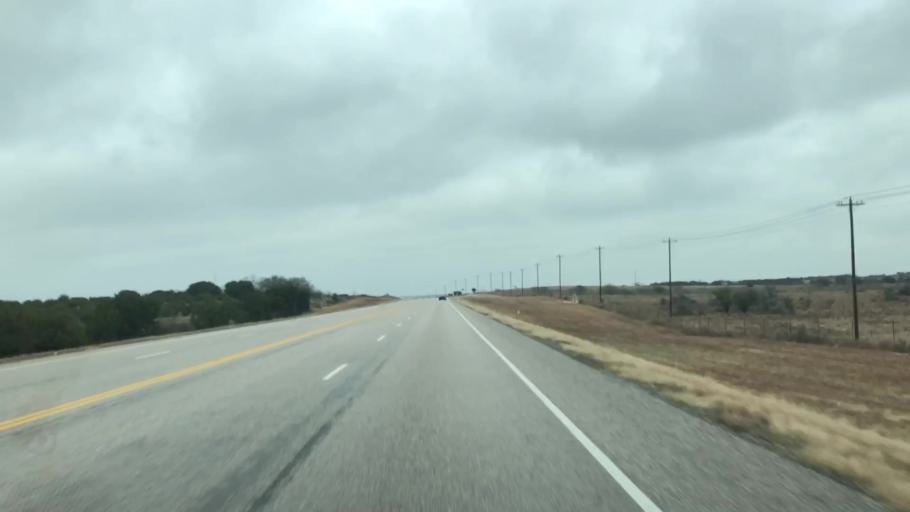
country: US
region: Texas
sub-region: Lampasas County
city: Lampasas
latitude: 30.9502
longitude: -98.2227
